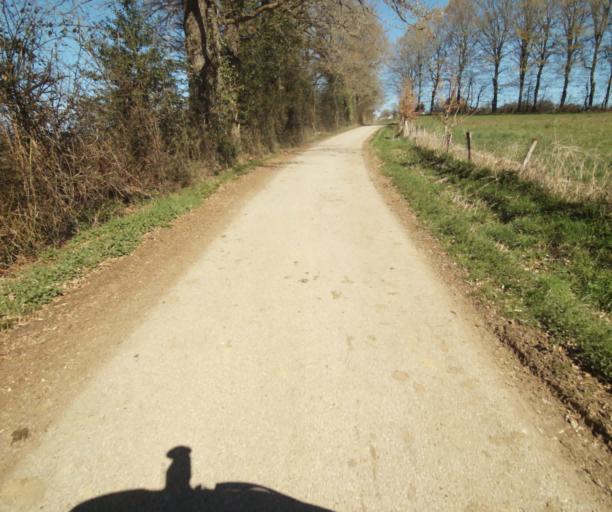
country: FR
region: Limousin
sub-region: Departement de la Correze
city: Chamboulive
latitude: 45.4222
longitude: 1.7217
